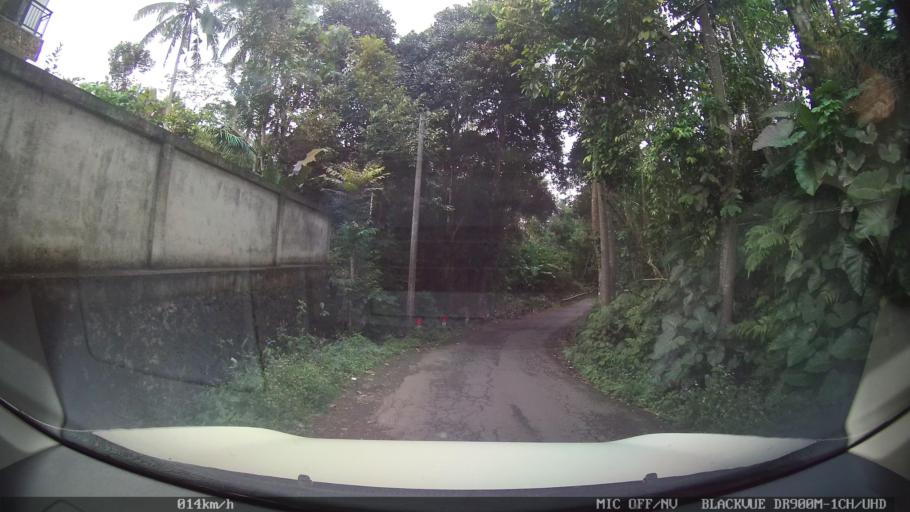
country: ID
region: Bali
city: Banjar Susut Kaja
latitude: -8.4374
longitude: 115.3238
